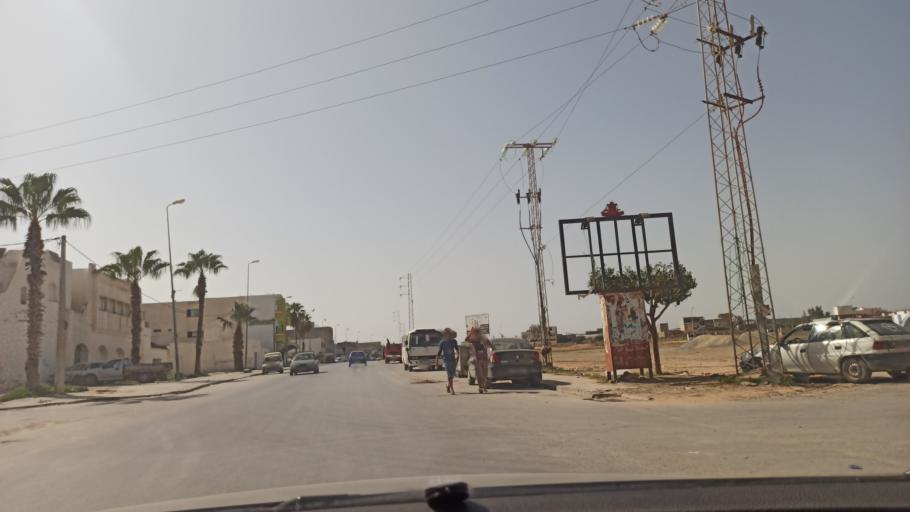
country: TN
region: Manouba
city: Manouba
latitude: 36.7651
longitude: 10.1105
